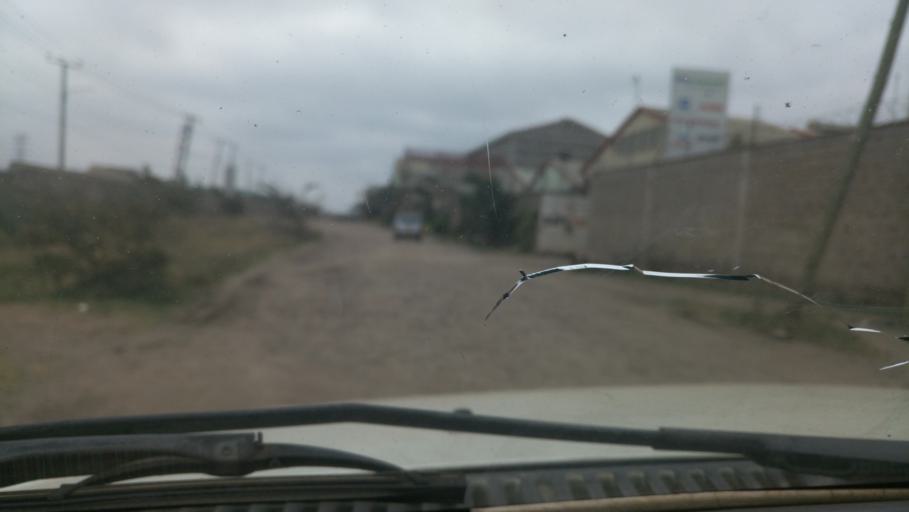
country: KE
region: Nairobi Area
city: Pumwani
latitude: -1.3351
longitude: 36.8695
